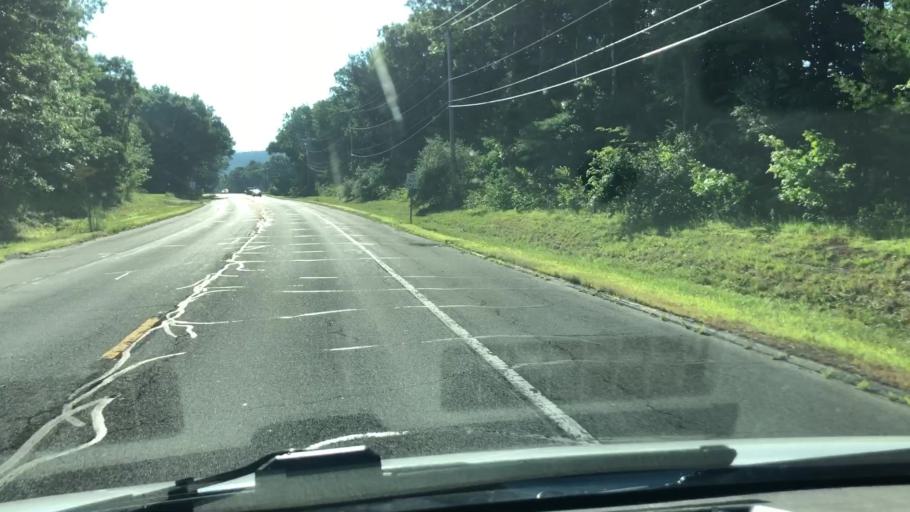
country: US
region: Massachusetts
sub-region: Franklin County
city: South Deerfield
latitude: 42.4669
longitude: -72.5983
